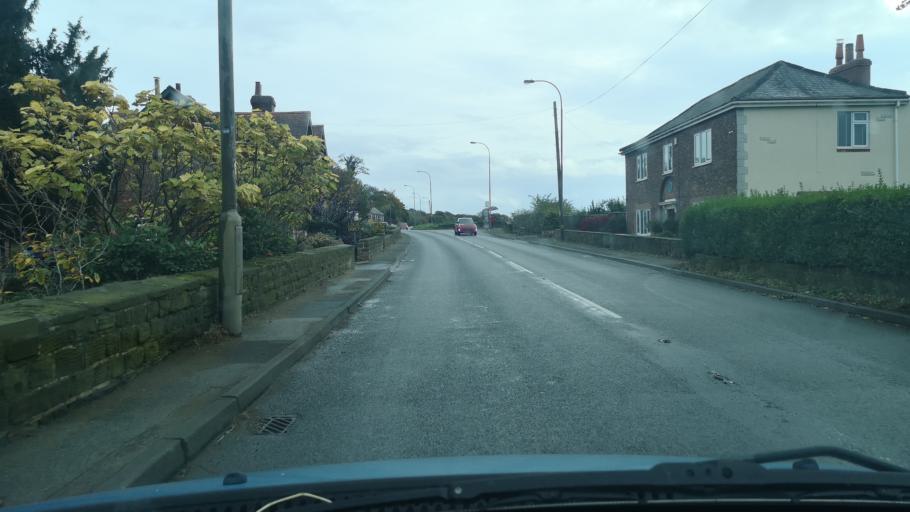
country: GB
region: England
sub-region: City and Borough of Wakefield
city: Sharlston
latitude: 53.6553
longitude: -1.4001
